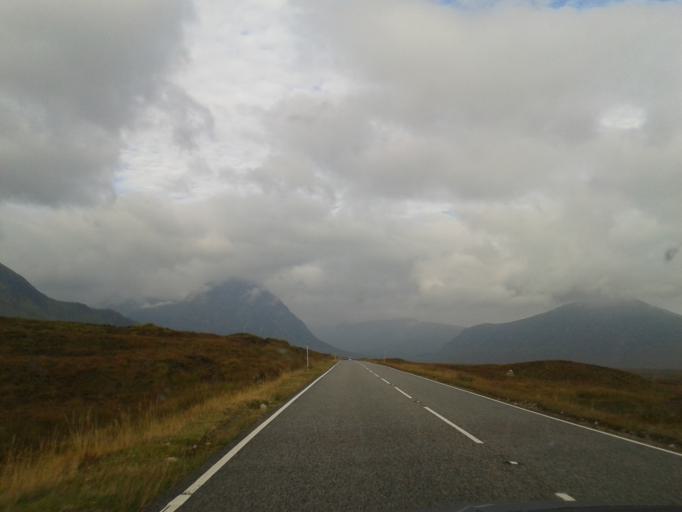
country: GB
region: Scotland
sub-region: Highland
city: Spean Bridge
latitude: 56.6333
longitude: -4.7949
